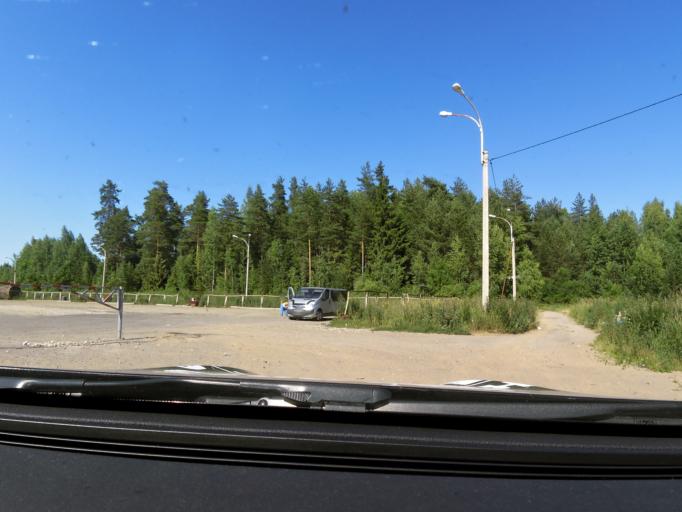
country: RU
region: Novgorod
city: Proletariy
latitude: 58.4177
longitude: 31.8404
